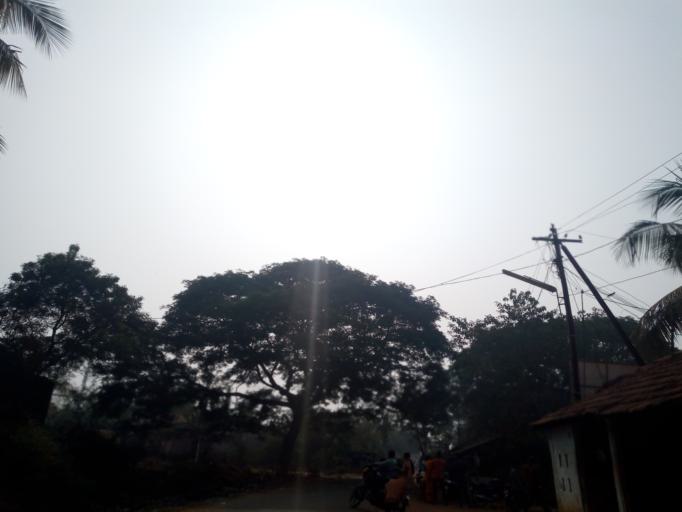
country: IN
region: Andhra Pradesh
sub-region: West Godavari
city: Tadepallegudem
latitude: 16.8120
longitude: 81.3643
